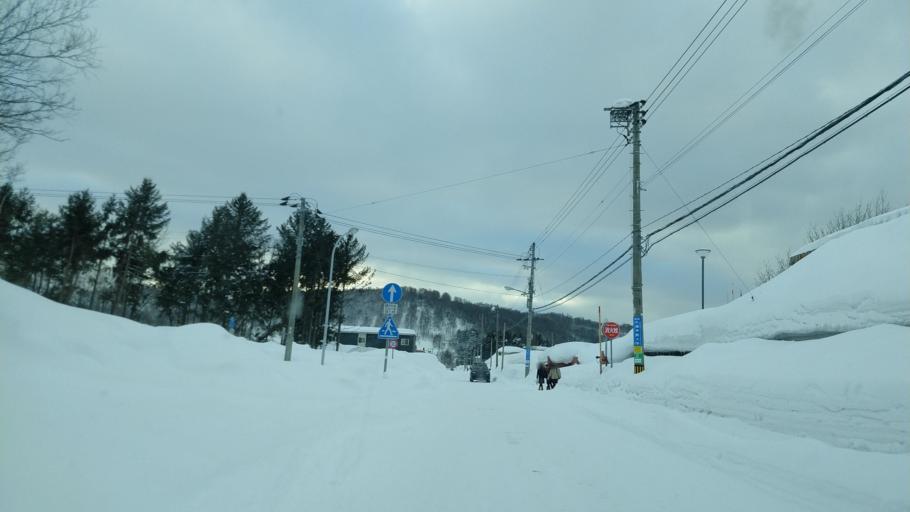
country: JP
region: Hokkaido
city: Niseko Town
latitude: 42.9091
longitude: 140.7503
